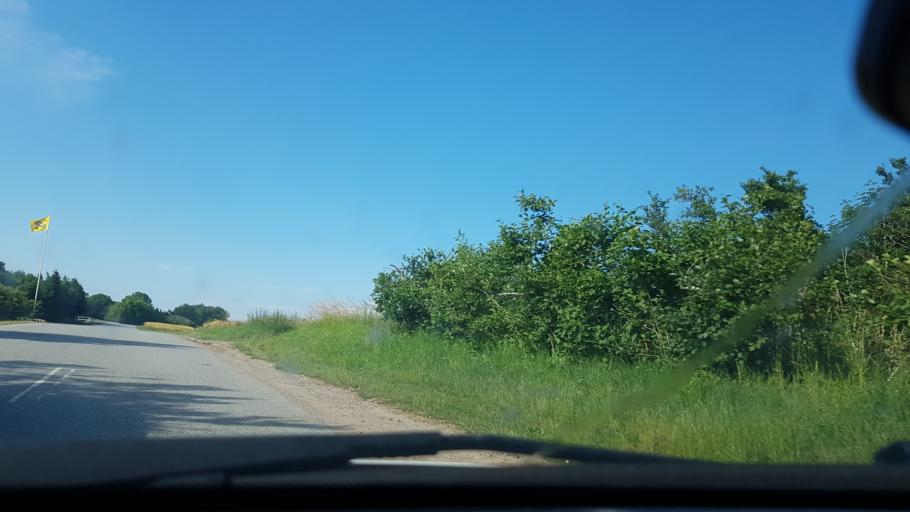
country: DK
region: Zealand
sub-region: Odsherred Kommune
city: Hojby
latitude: 55.8935
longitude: 11.6156
